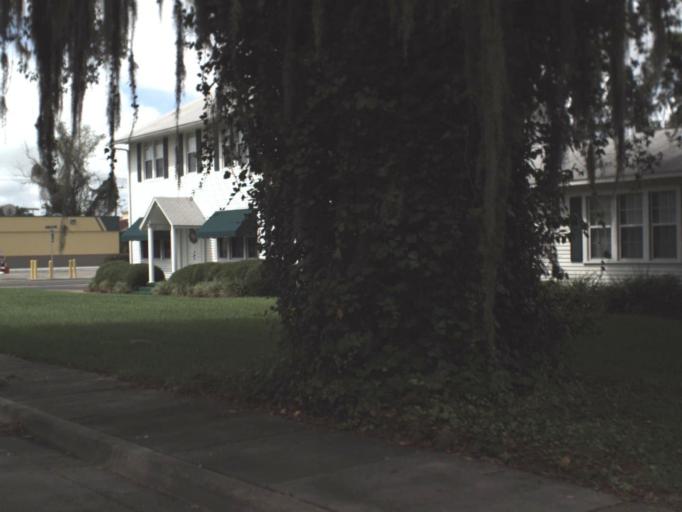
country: US
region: Florida
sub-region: Columbia County
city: Lake City
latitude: 30.1844
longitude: -82.6371
